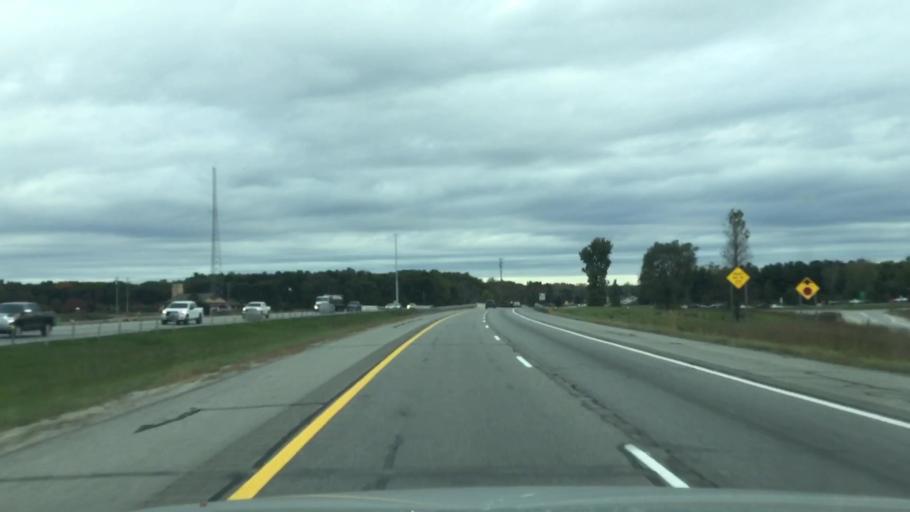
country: US
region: Michigan
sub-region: Livingston County
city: Whitmore Lake
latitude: 42.4649
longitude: -83.7558
